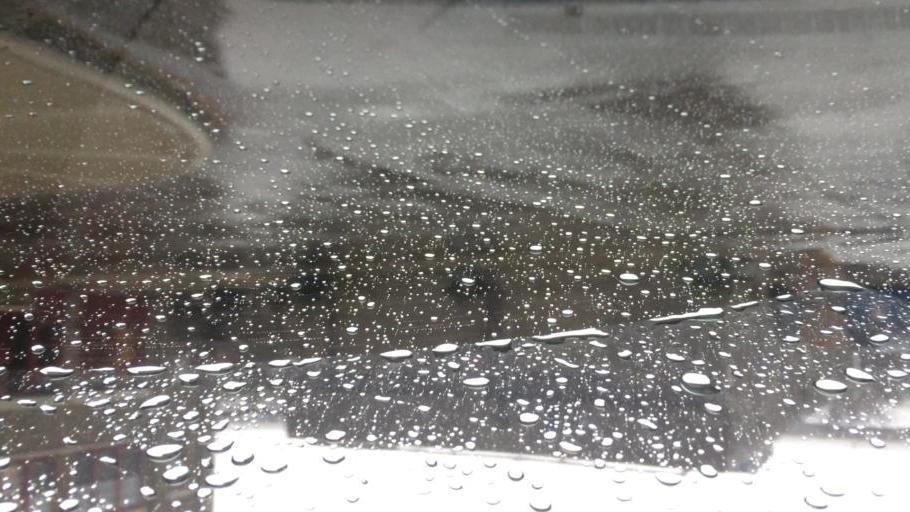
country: US
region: Ohio
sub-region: Summit County
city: Akron
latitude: 41.0917
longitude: -81.5170
